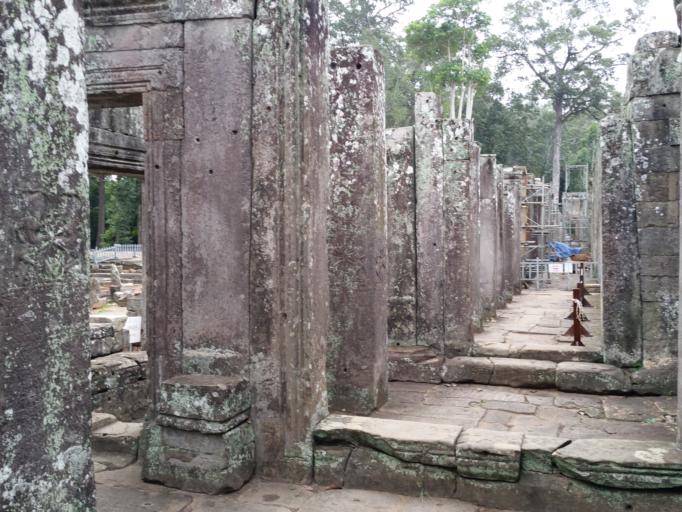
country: KH
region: Siem Reap
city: Siem Reap
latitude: 13.4417
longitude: 103.8595
